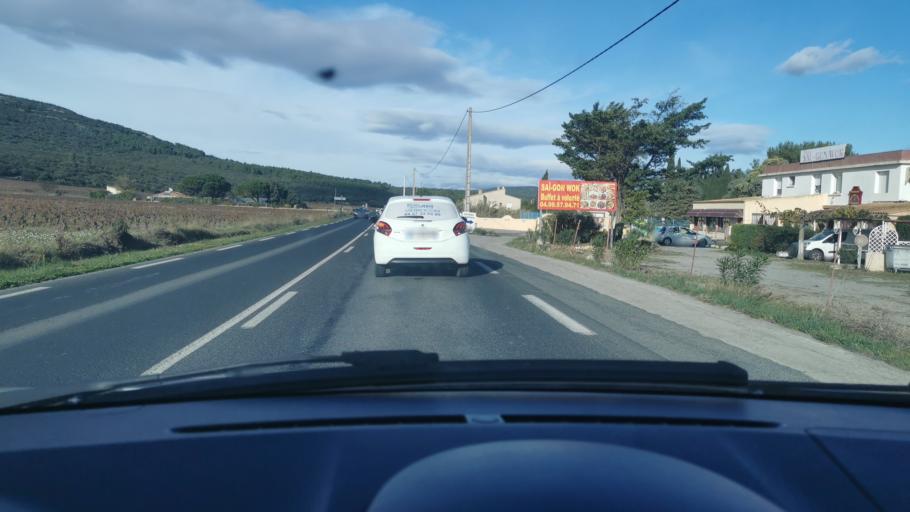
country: FR
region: Languedoc-Roussillon
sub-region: Departement de l'Herault
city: Vic-la-Gardiole
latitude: 43.4814
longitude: 3.7729
